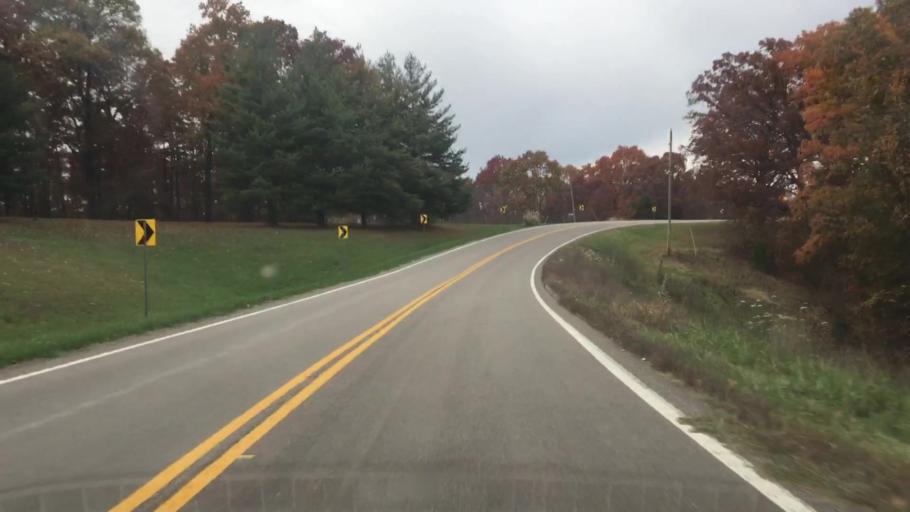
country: US
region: Missouri
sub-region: Gasconade County
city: Hermann
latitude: 38.7155
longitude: -91.6405
